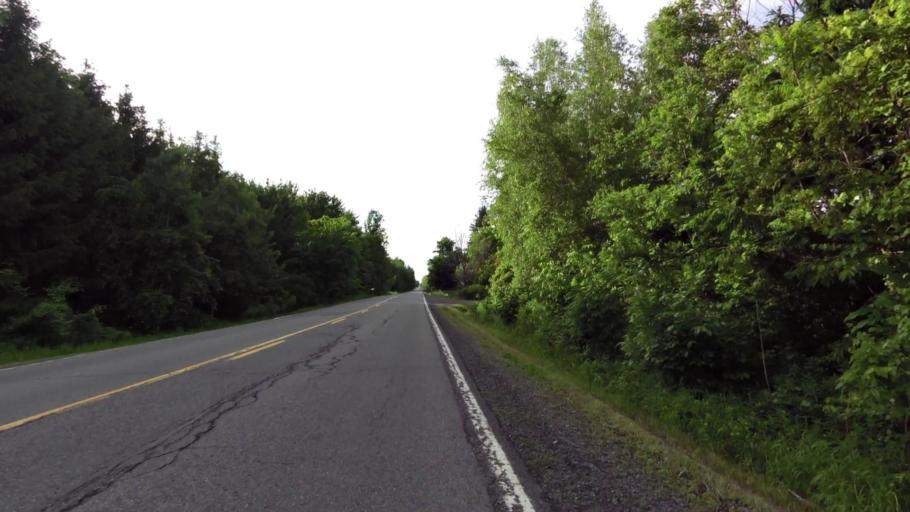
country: CA
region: Ontario
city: Ottawa
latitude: 45.1996
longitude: -75.5910
